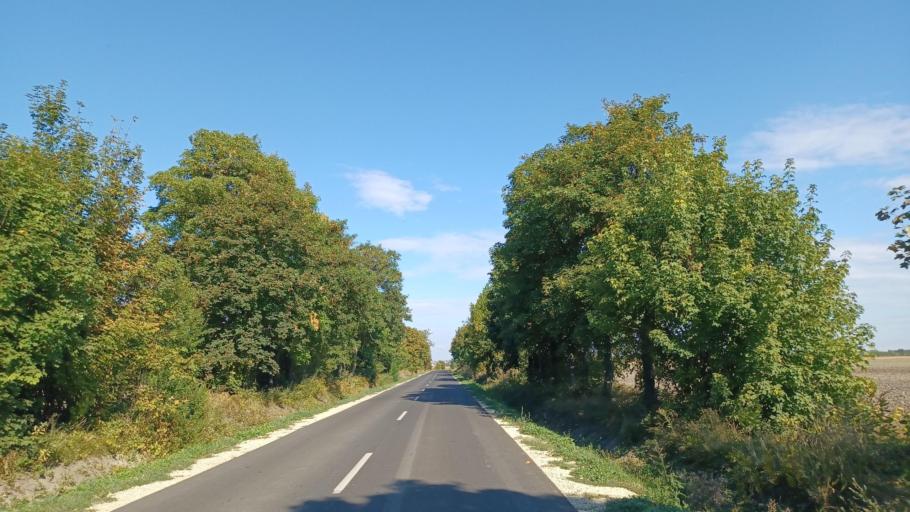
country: HU
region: Tolna
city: Dunaszentgyorgy
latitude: 46.5020
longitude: 18.8257
